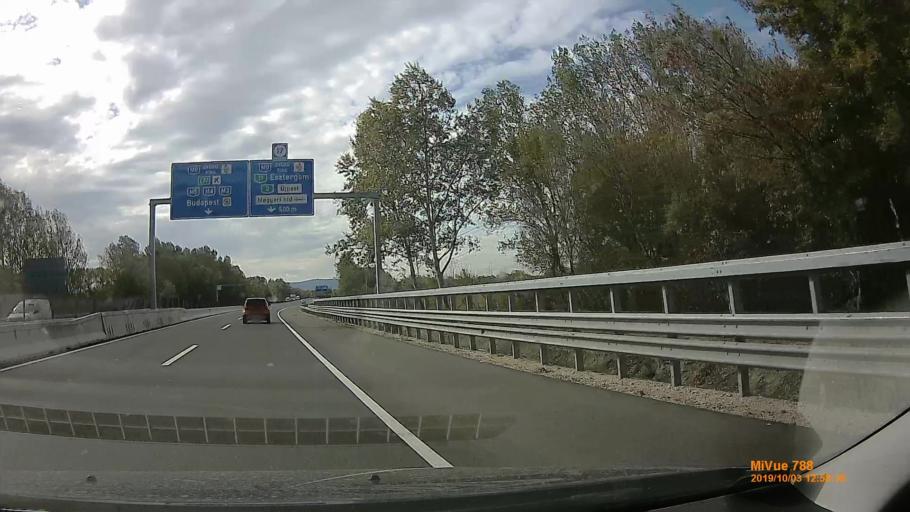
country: HU
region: Pest
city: Dunakeszi
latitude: 47.5987
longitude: 19.1483
